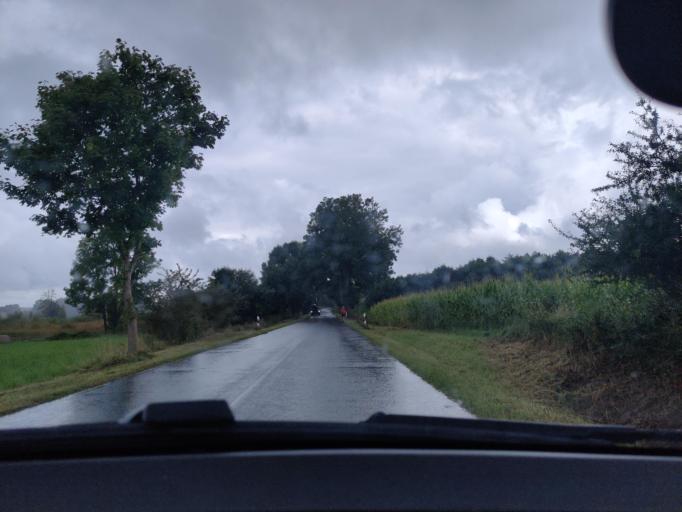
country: DE
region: Mecklenburg-Vorpommern
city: Wesenberg
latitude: 53.2754
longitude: 12.9908
